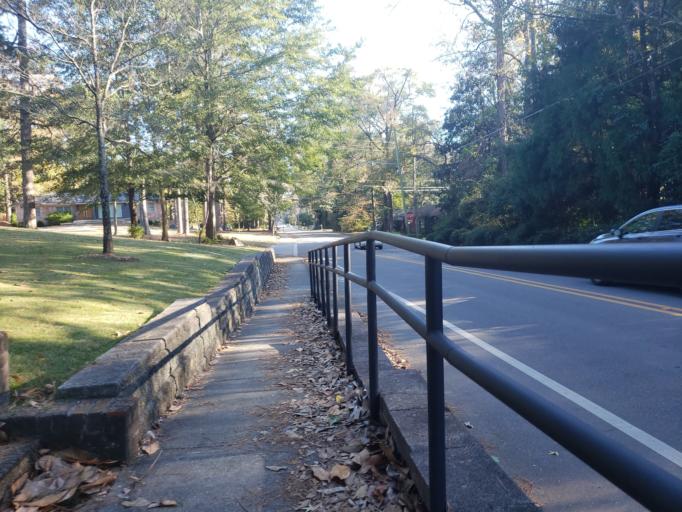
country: US
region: Alabama
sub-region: Lee County
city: Auburn
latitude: 32.5898
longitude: -85.4794
